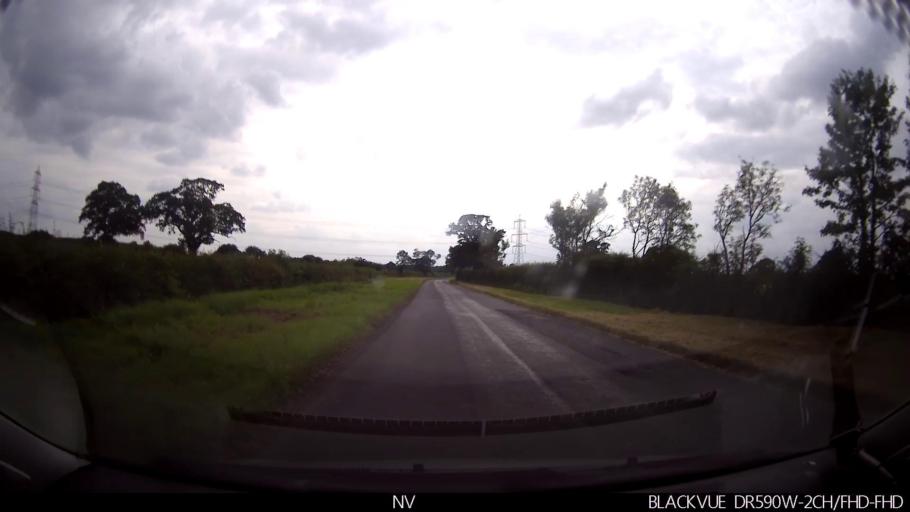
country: GB
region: England
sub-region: North Yorkshire
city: Strensall
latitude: 54.0495
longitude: -0.9719
